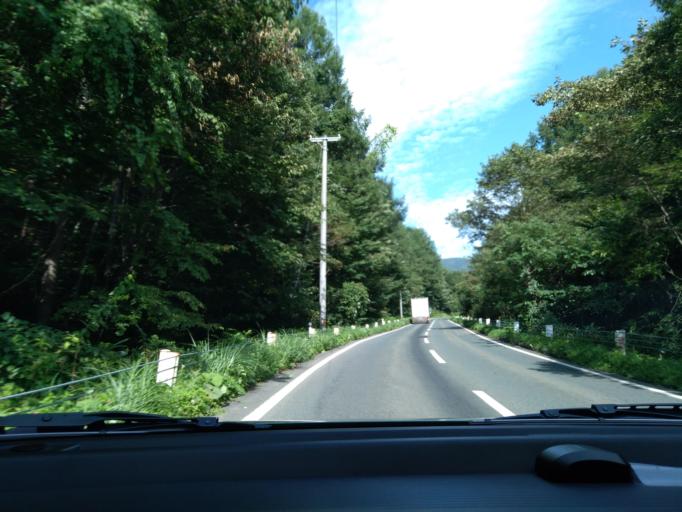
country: JP
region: Iwate
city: Shizukuishi
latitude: 39.6396
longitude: 141.0119
